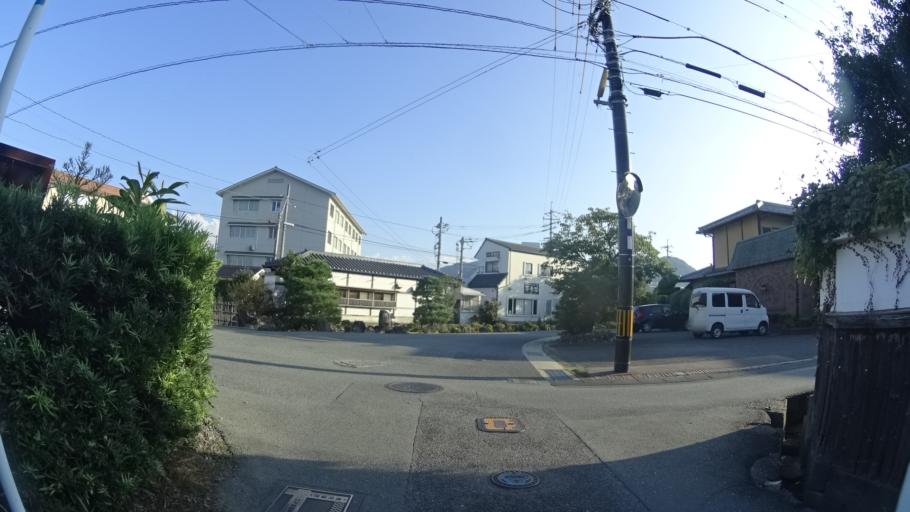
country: JP
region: Yamaguchi
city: Hagi
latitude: 34.4107
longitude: 131.3946
